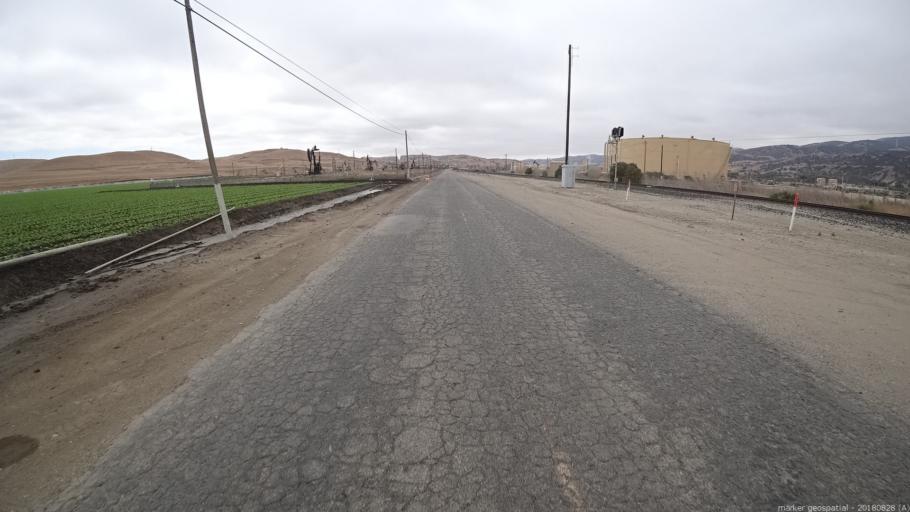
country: US
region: California
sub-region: San Luis Obispo County
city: Lake Nacimiento
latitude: 35.9685
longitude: -120.8719
